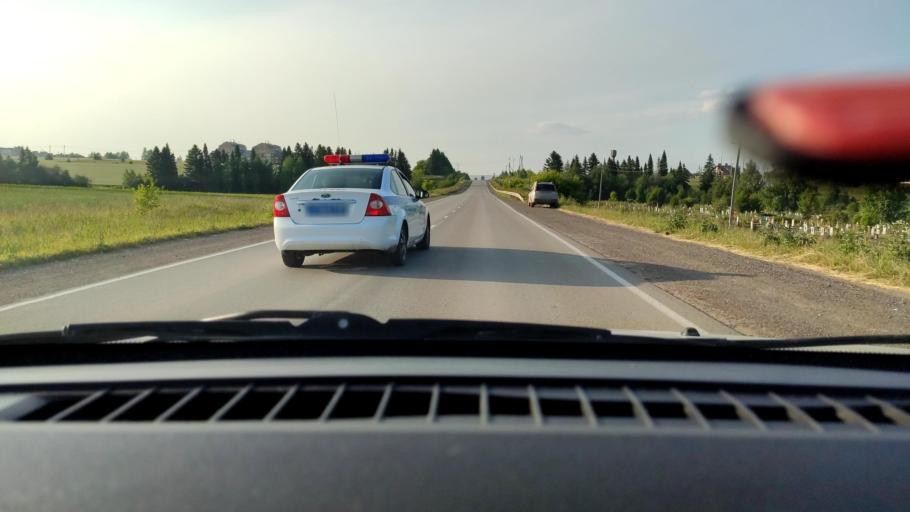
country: RU
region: Perm
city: Lobanovo
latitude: 57.8547
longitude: 56.2961
